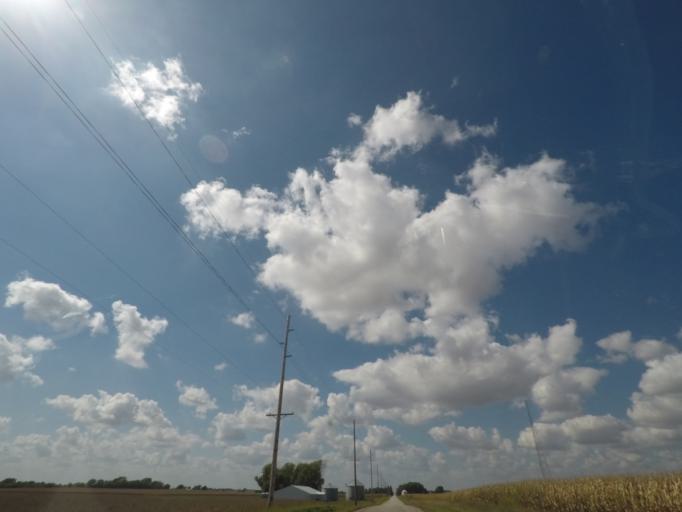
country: US
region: Iowa
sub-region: Story County
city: Nevada
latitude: 42.0344
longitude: -93.3829
